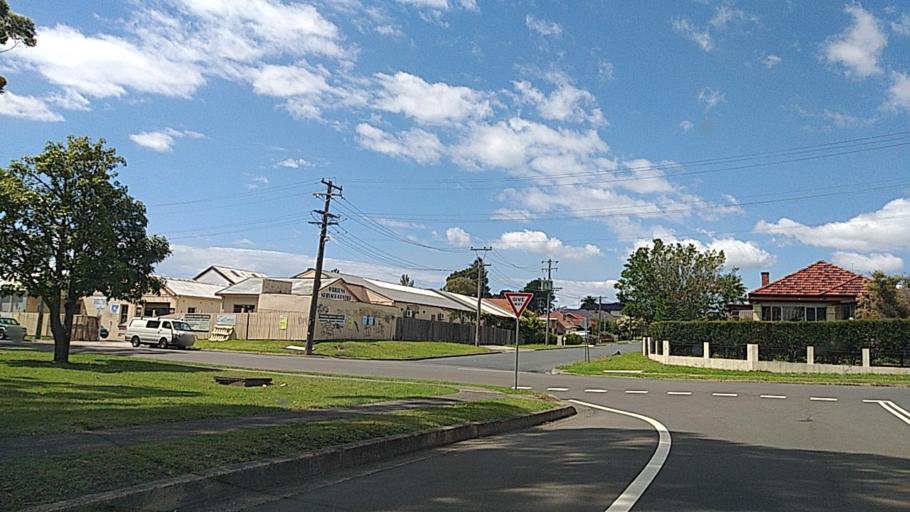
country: AU
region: New South Wales
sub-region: Wollongong
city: Corrimal
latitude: -34.3744
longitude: 150.8951
